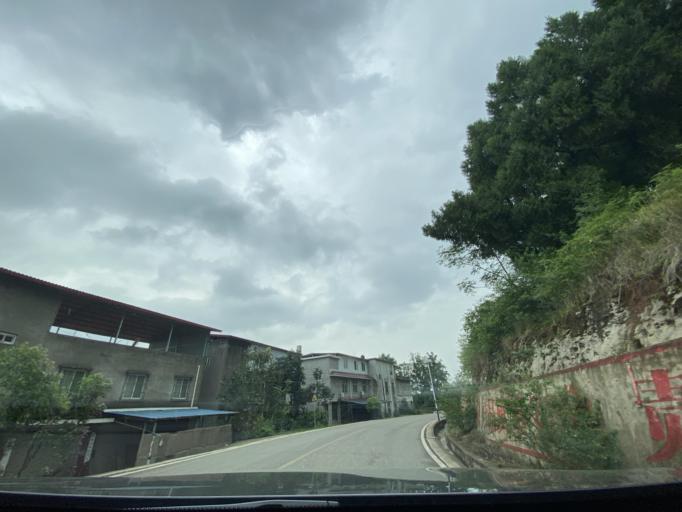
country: CN
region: Sichuan
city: Jiancheng
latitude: 30.5399
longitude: 104.5208
